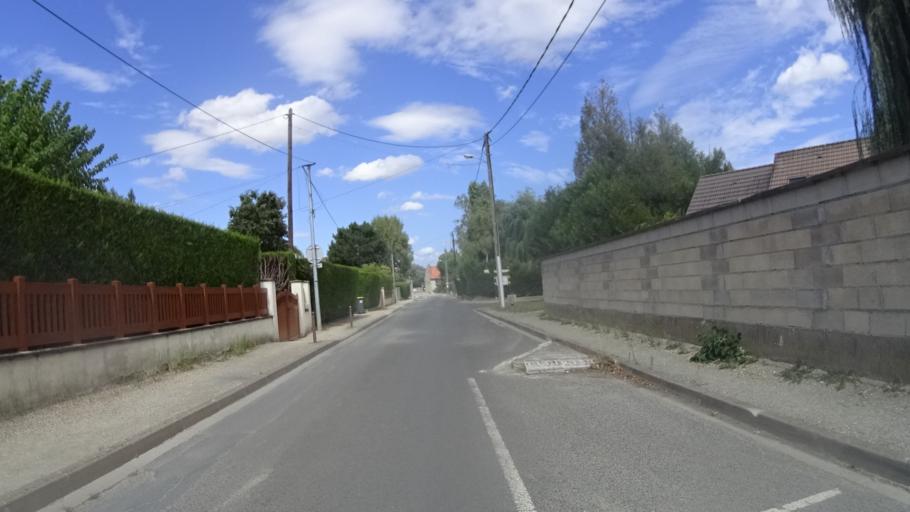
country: FR
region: Ile-de-France
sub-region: Departement de l'Essonne
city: Maisse
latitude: 48.3949
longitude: 2.3962
